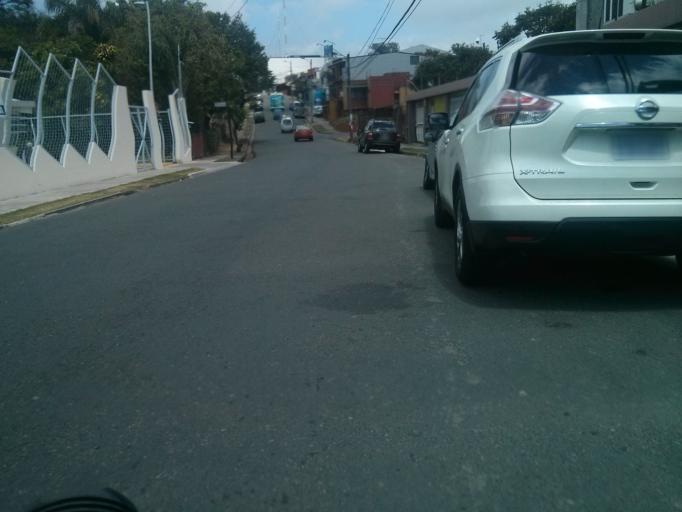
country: CR
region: San Jose
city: San Pedro
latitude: 9.9260
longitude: -84.0546
